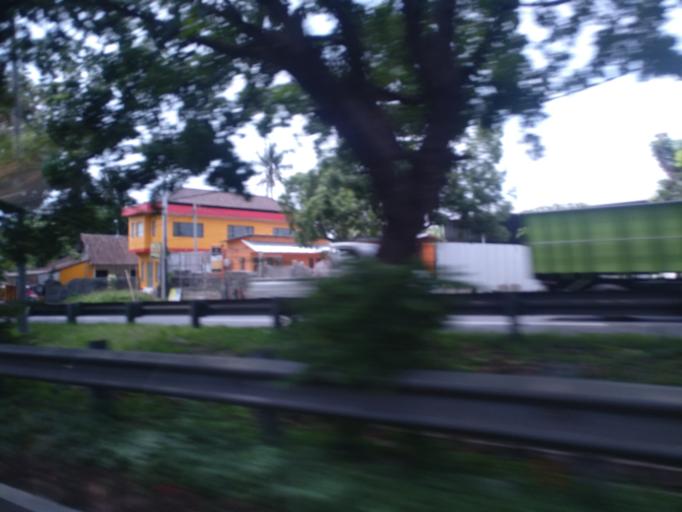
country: ID
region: Bali
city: Banjar Pasekan
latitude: -8.6094
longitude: 115.3136
